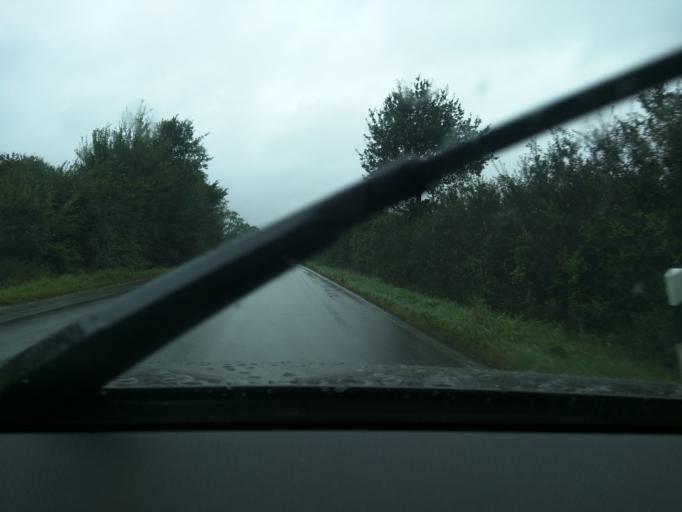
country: DE
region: Schleswig-Holstein
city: Wangelau
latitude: 53.4530
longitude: 10.5526
